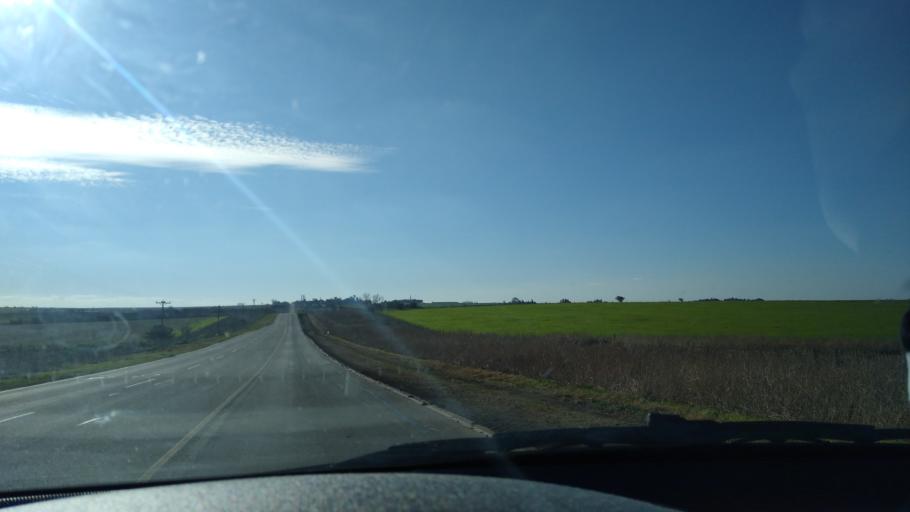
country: AR
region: Entre Rios
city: Aranguren
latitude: -32.3820
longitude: -60.3363
